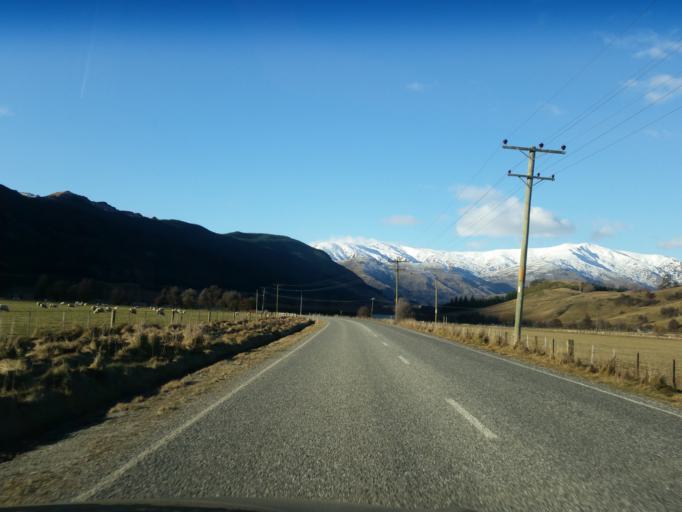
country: NZ
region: Otago
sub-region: Queenstown-Lakes District
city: Arrowtown
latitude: -44.9512
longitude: 168.7543
